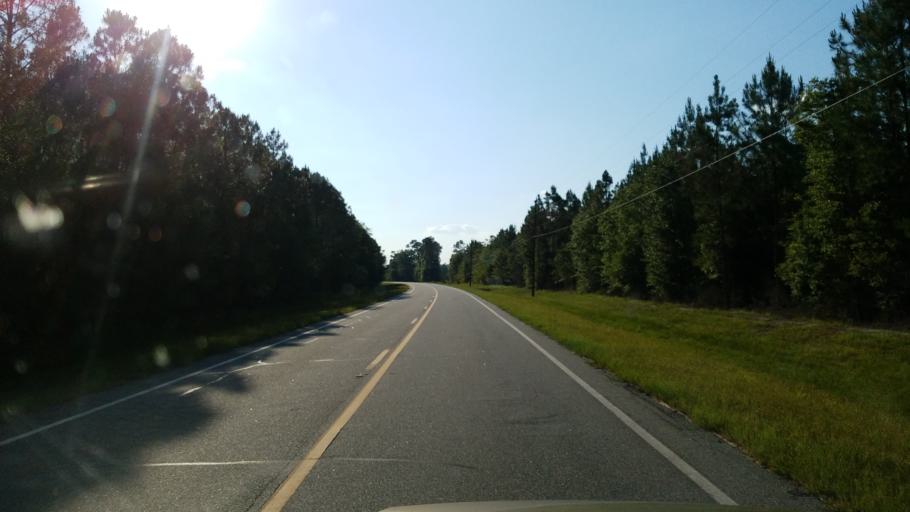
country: US
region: Georgia
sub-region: Lanier County
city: Lakeland
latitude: 30.9016
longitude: -83.0676
